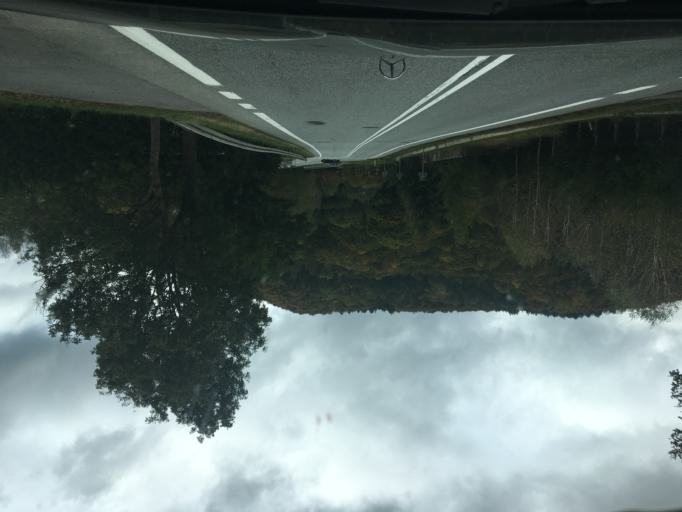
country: PL
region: Subcarpathian Voivodeship
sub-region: Powiat krosnienski
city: Dukla
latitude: 49.4660
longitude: 21.6965
